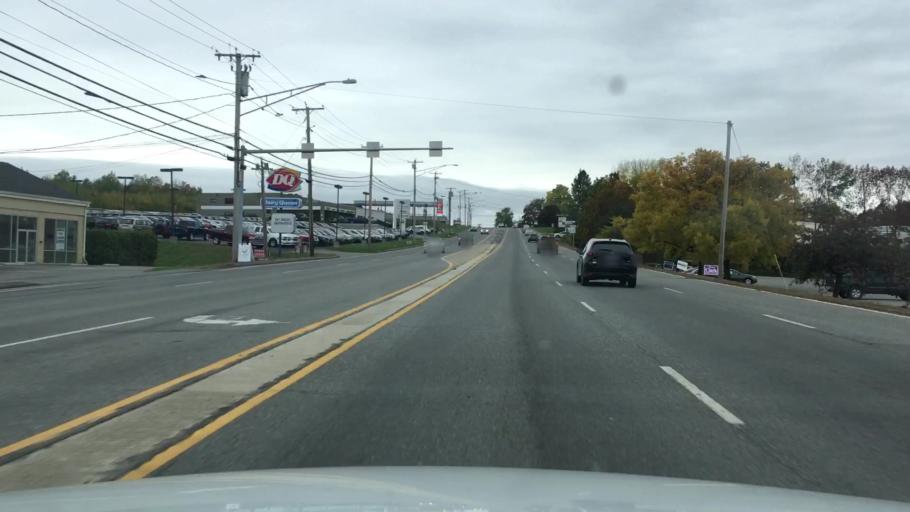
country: US
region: Maine
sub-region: Kennebec County
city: Waterville
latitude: 44.5436
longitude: -69.6662
